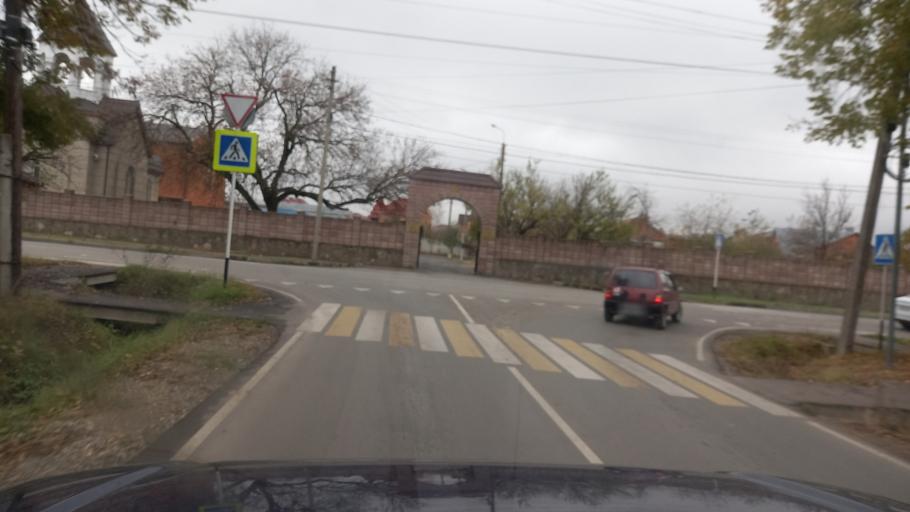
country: RU
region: Adygeya
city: Maykop
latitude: 44.6003
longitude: 40.0730
